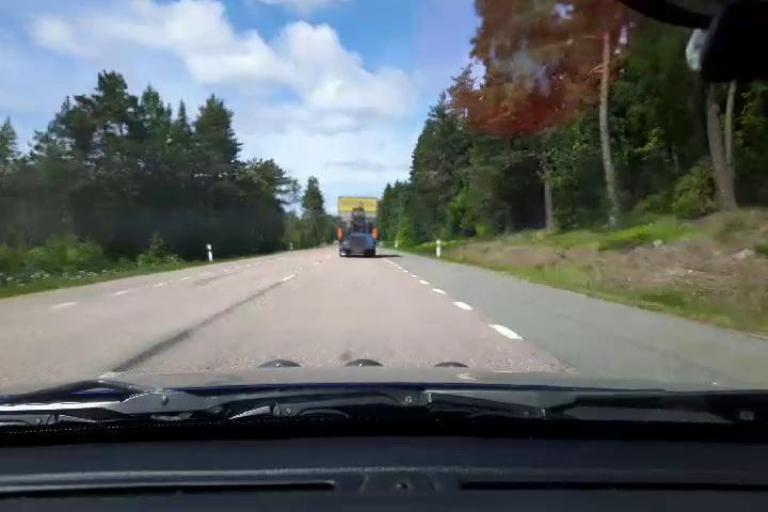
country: SE
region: Uppsala
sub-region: Osthammars Kommun
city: Bjorklinge
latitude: 60.1022
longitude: 17.5511
